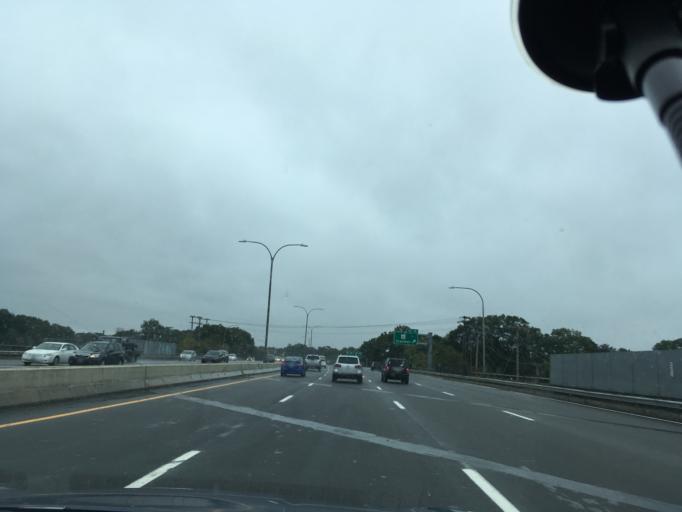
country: US
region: Rhode Island
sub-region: Providence County
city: Cranston
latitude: 41.7868
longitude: -71.4212
